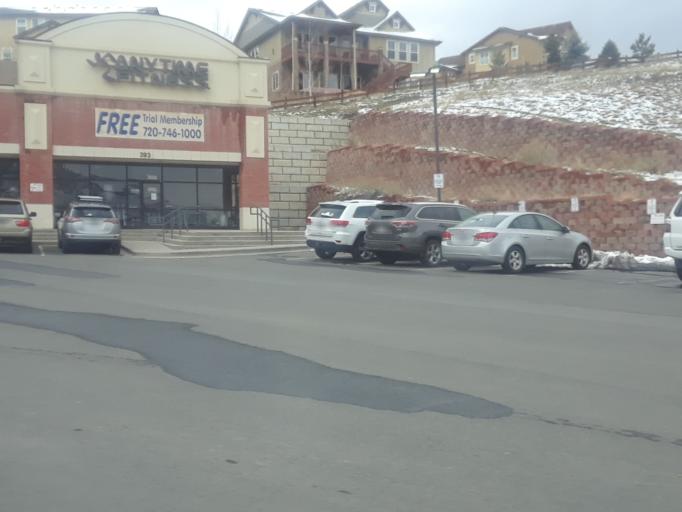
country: US
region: Colorado
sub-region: Jefferson County
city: Golden
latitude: 39.7683
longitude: -105.2346
